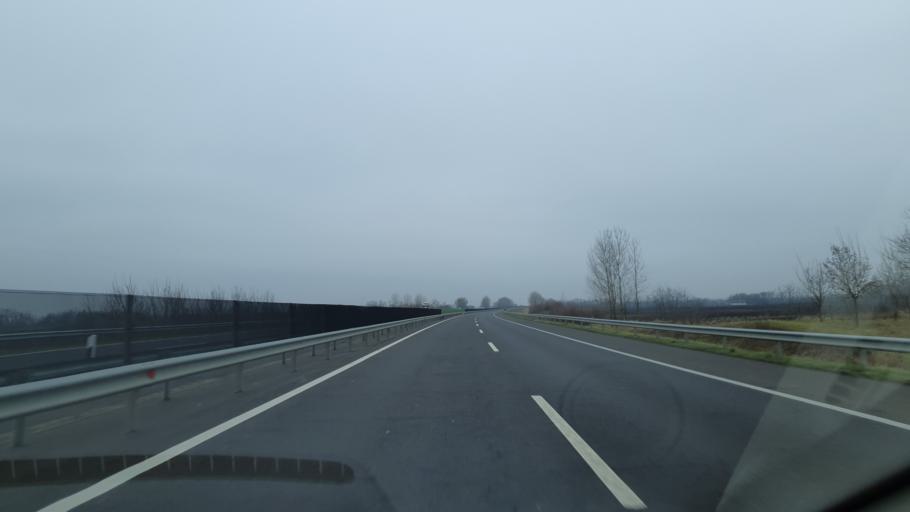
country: HU
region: Szabolcs-Szatmar-Bereg
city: Kalmanhaza
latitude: 47.8986
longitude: 21.5377
